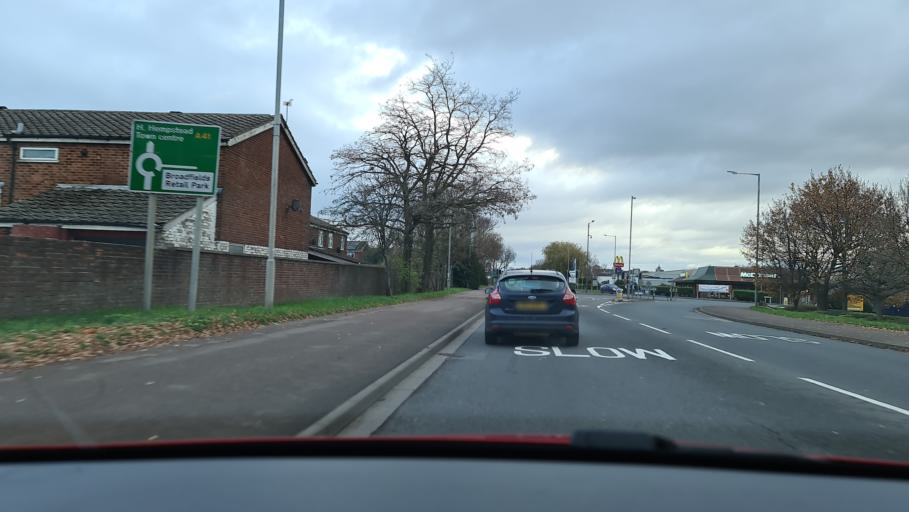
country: GB
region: England
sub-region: Buckinghamshire
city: Aylesbury
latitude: 51.8250
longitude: -0.8350
